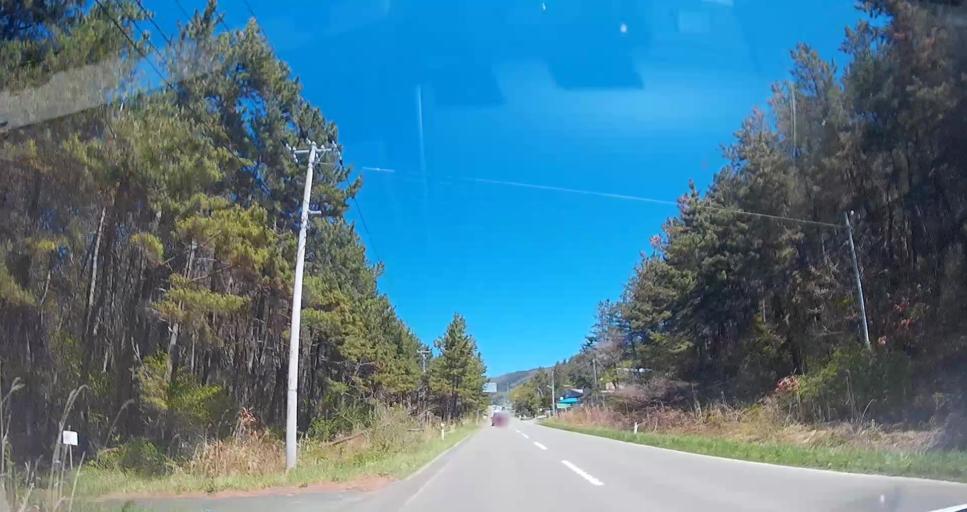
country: JP
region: Aomori
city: Mutsu
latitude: 41.3774
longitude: 141.3946
